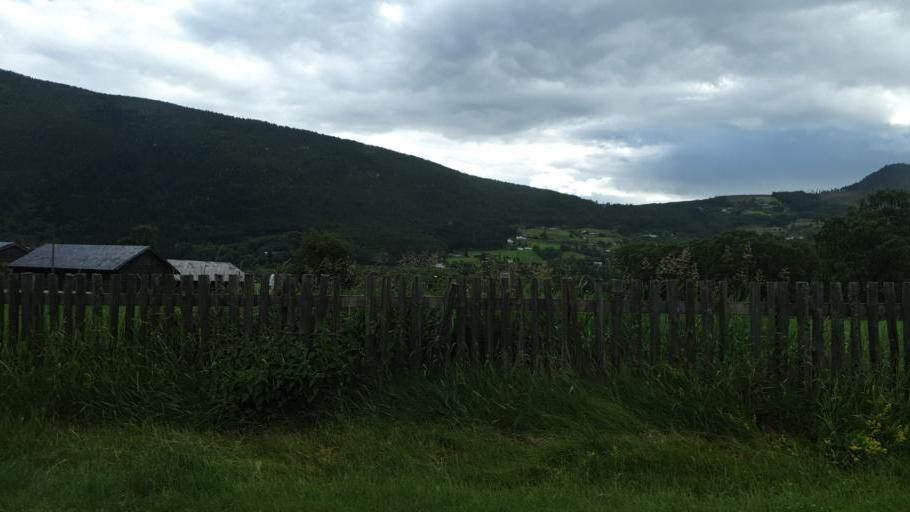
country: NO
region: Oppland
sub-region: Sel
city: Otta
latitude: 61.8493
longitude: 9.4210
